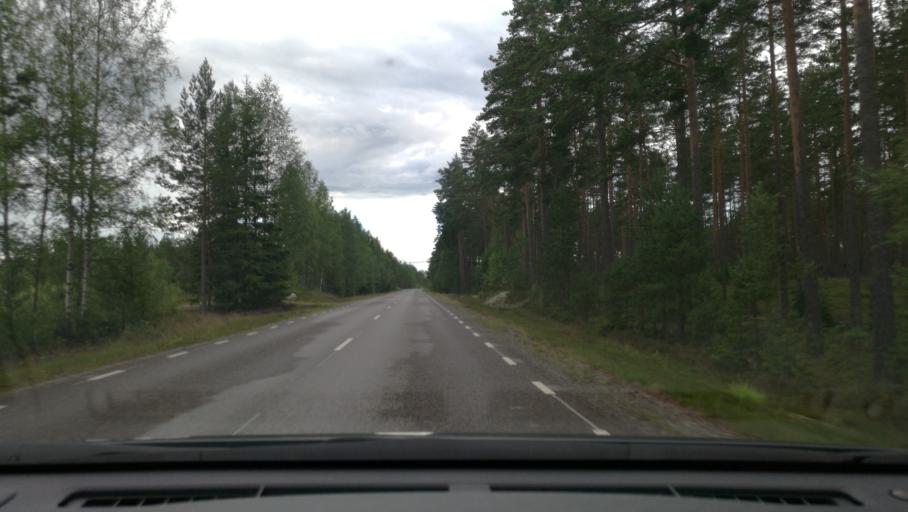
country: SE
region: OEstergoetland
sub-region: Norrkopings Kommun
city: Svartinge
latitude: 58.7336
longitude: 15.9533
